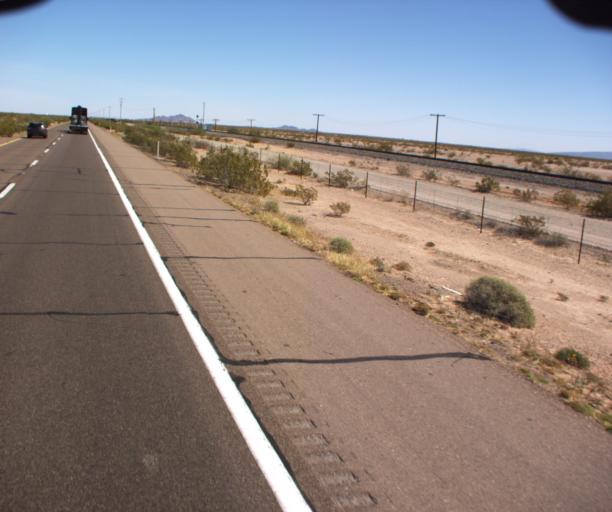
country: US
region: Arizona
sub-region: Yuma County
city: Wellton
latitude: 32.7591
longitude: -113.6389
